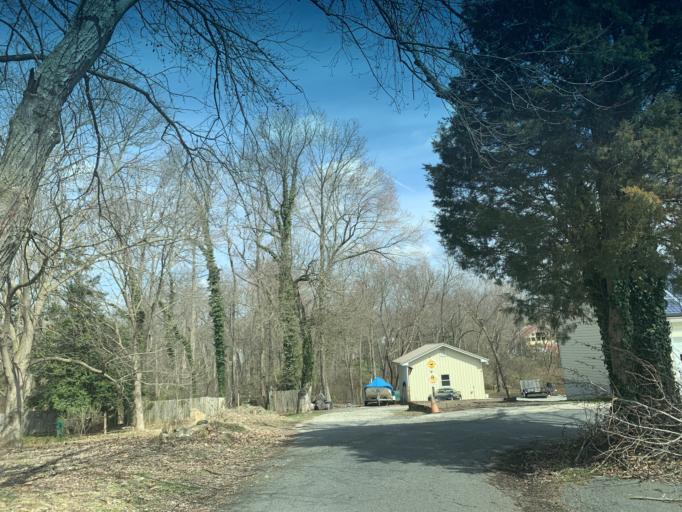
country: US
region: Maryland
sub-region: Cecil County
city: Charlestown
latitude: 39.5723
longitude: -75.9790
